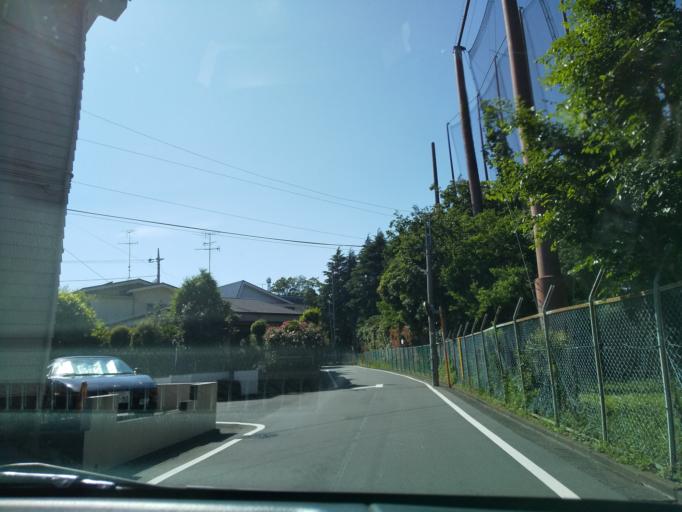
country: JP
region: Kanagawa
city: Zama
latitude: 35.5429
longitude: 139.3920
